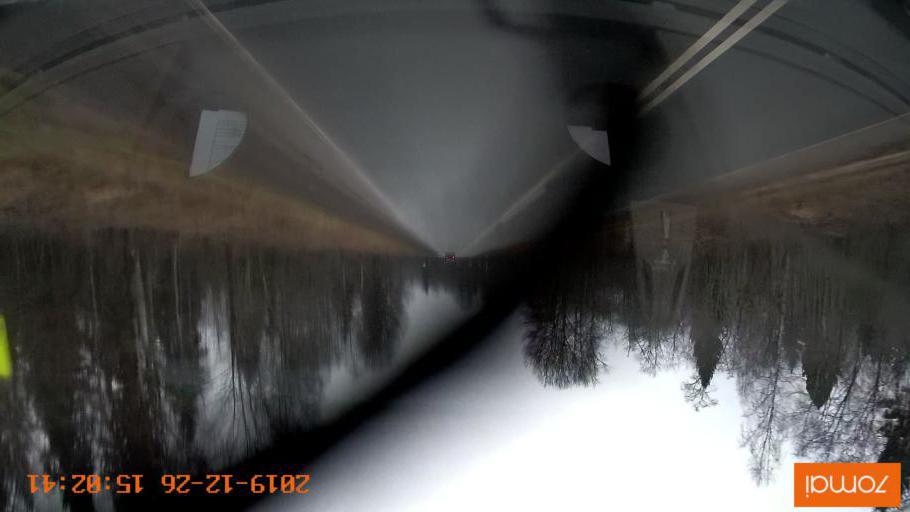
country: RU
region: Jaroslavl
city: Rybinsk
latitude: 58.2222
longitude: 38.8756
